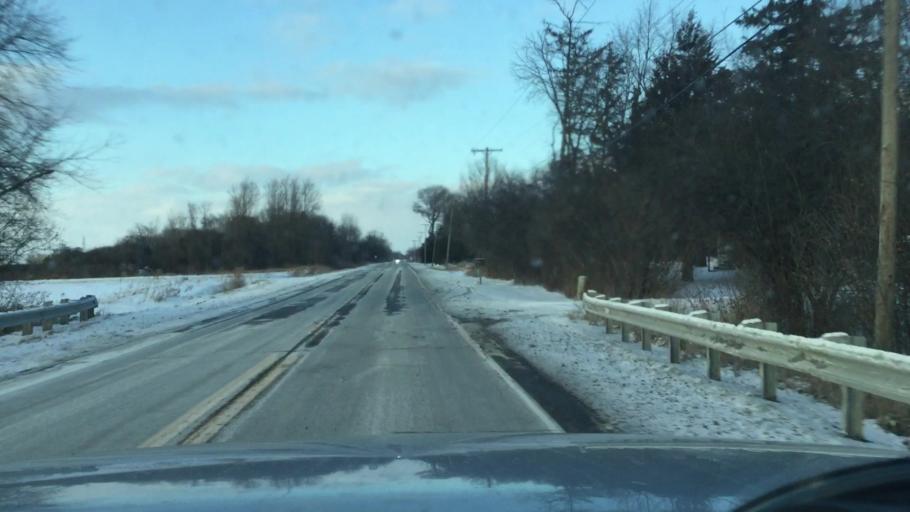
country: US
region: Michigan
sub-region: Saginaw County
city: Saginaw
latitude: 43.3786
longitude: -83.9354
